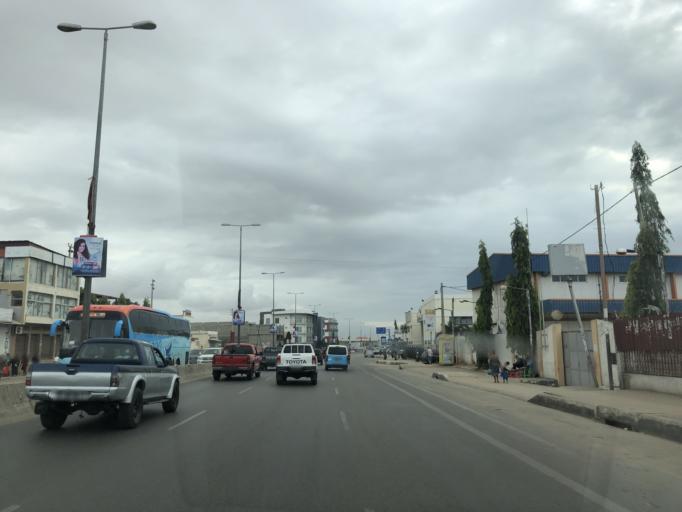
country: AO
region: Luanda
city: Luanda
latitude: -8.8874
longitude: 13.2051
